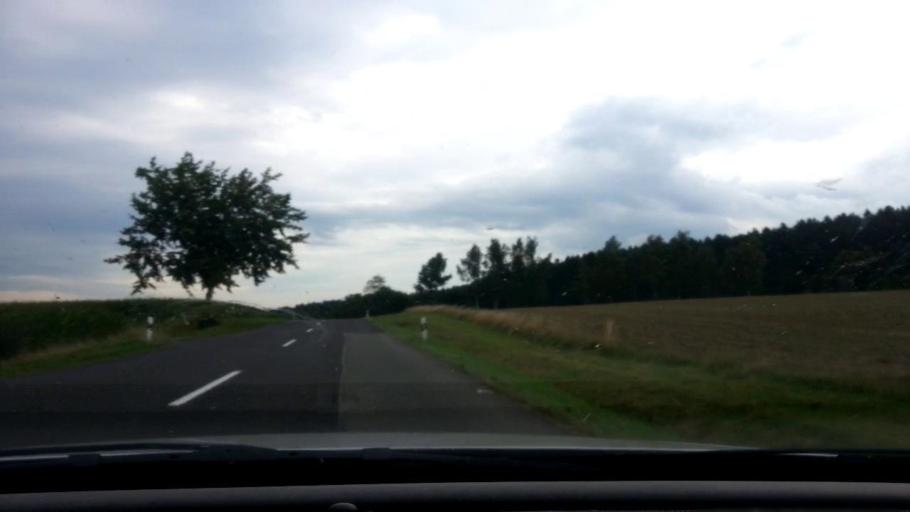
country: DE
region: Bavaria
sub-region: Upper Palatinate
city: Kulmain
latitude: 49.8842
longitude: 11.9317
